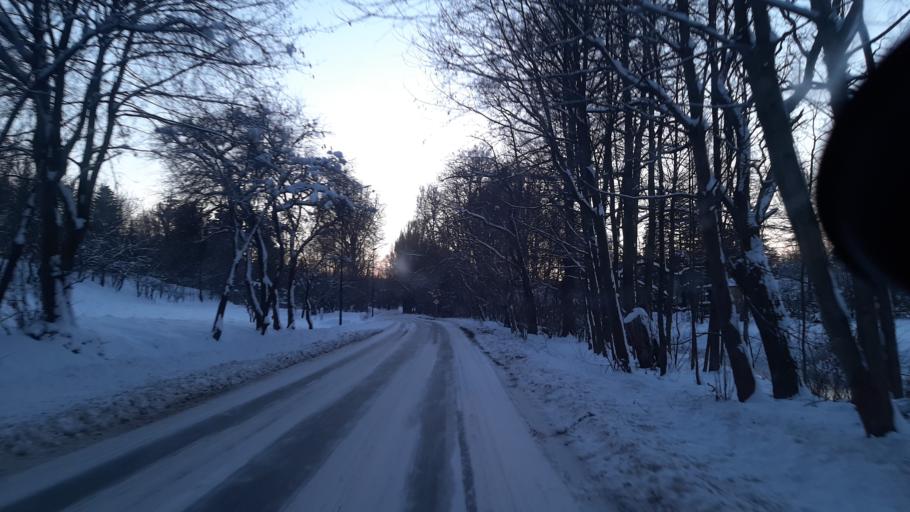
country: PL
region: Lublin Voivodeship
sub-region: Powiat lubelski
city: Lublin
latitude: 51.3133
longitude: 22.5780
